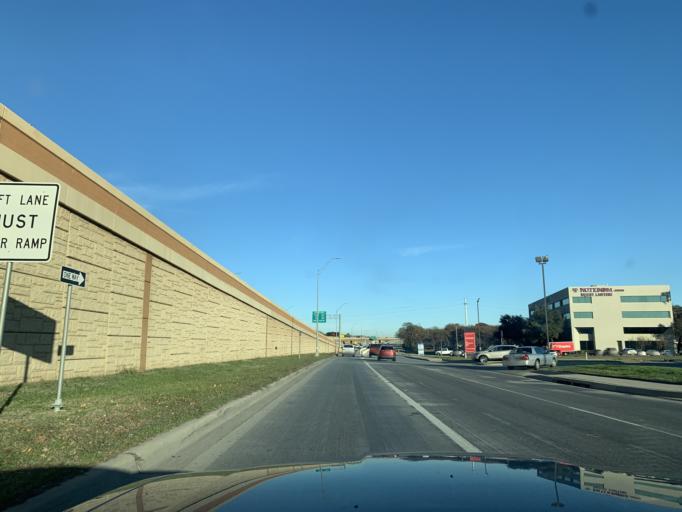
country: US
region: Texas
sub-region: Tarrant County
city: Hurst
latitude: 32.8388
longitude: -97.1850
